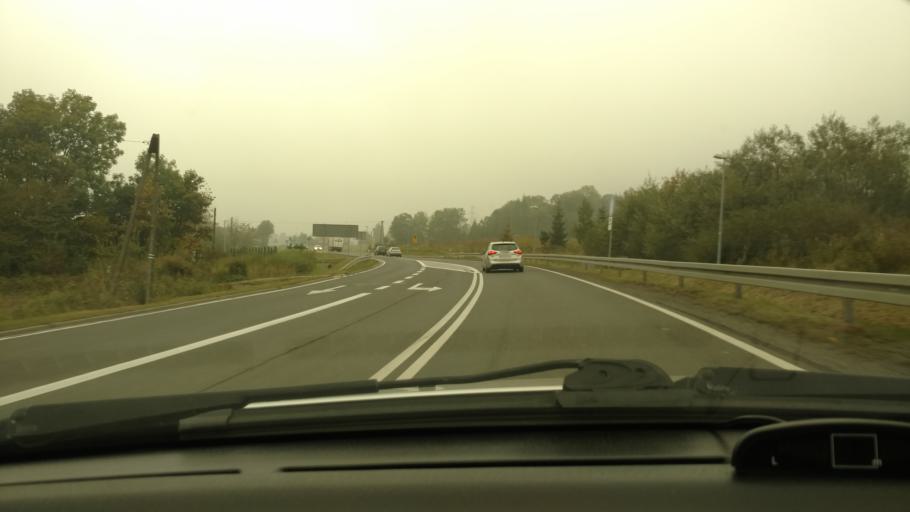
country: PL
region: Lesser Poland Voivodeship
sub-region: Powiat nowosadecki
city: Kamionka Wielka
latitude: 49.6169
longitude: 20.8666
